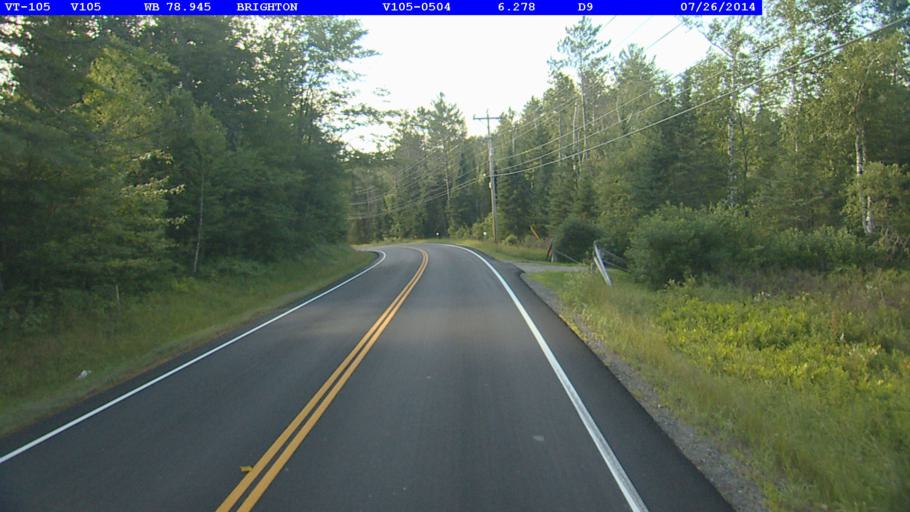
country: US
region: Vermont
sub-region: Caledonia County
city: Lyndonville
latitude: 44.8062
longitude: -71.8507
